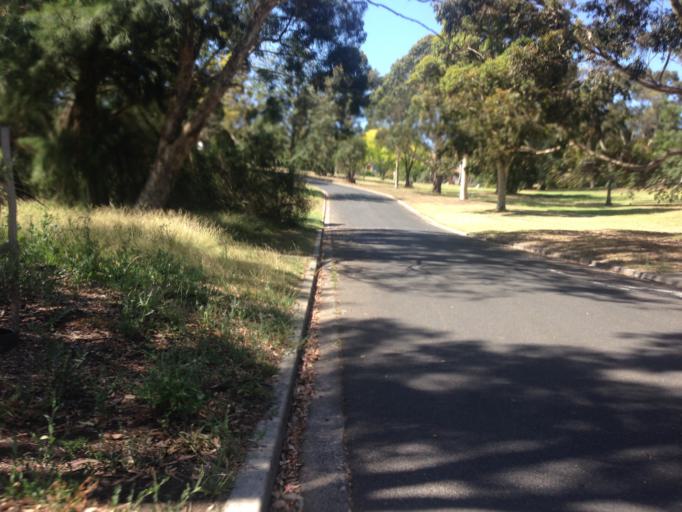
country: AU
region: Victoria
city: Ivanhoe East
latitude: -37.7783
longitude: 145.0617
